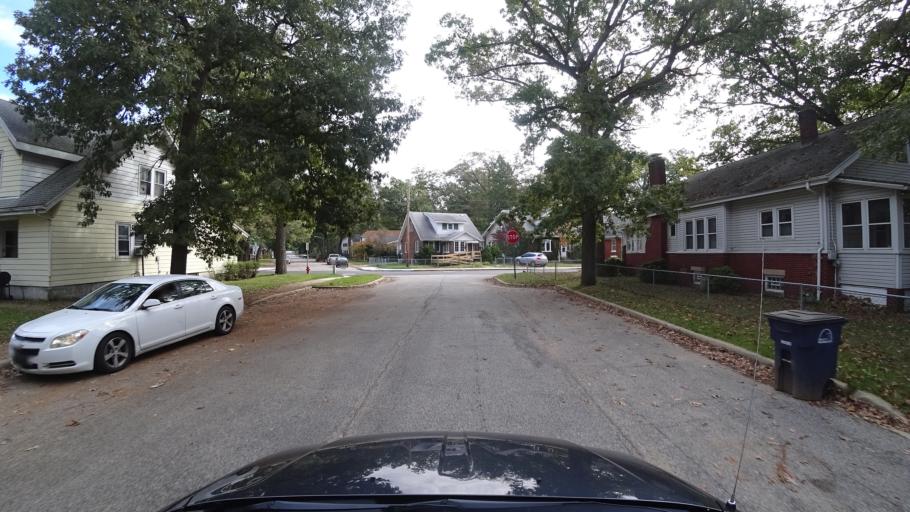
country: US
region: Indiana
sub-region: LaPorte County
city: Michigan City
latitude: 41.7162
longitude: -86.8835
